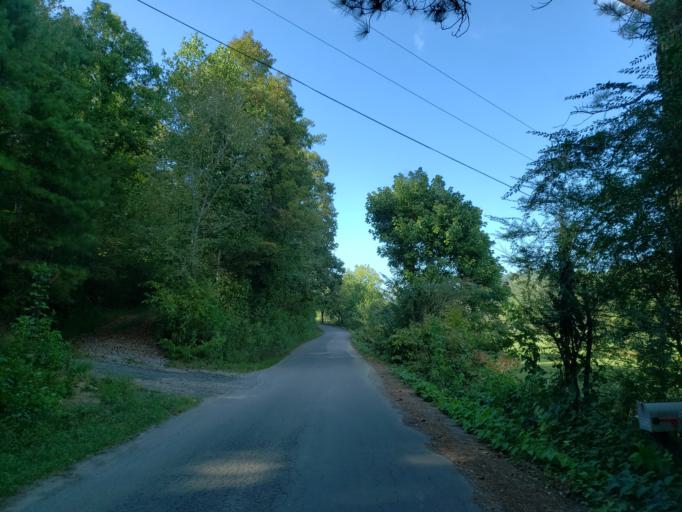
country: US
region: Georgia
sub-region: Gilmer County
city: Ellijay
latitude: 34.5832
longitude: -84.5098
